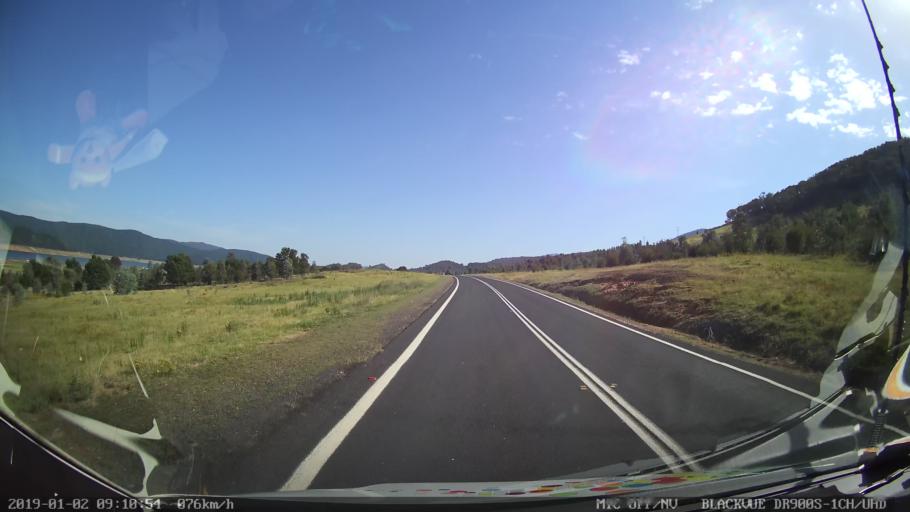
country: AU
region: New South Wales
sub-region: Tumut Shire
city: Tumut
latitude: -35.5171
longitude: 148.2686
